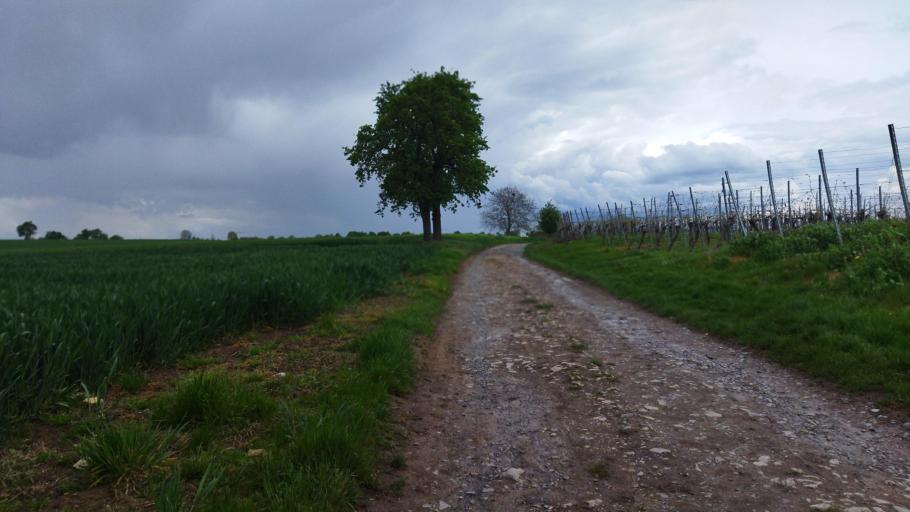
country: DE
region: Baden-Wuerttemberg
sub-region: Regierungsbezirk Stuttgart
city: Mundelsheim
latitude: 49.0053
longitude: 9.1950
